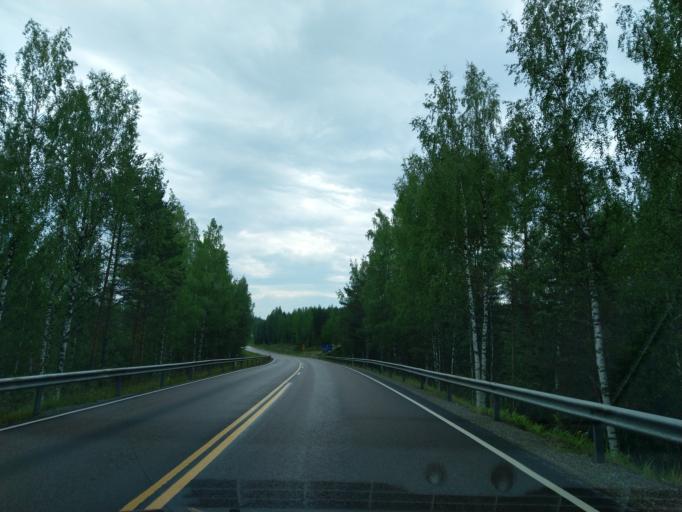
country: FI
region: Southern Savonia
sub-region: Savonlinna
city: Punkaharju
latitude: 61.6787
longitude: 29.4132
